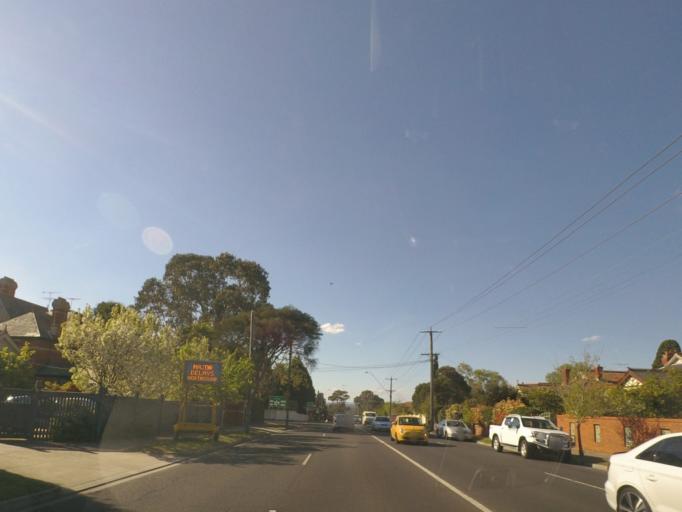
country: AU
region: Victoria
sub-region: Boroondara
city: Kew
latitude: -37.8009
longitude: 145.0299
